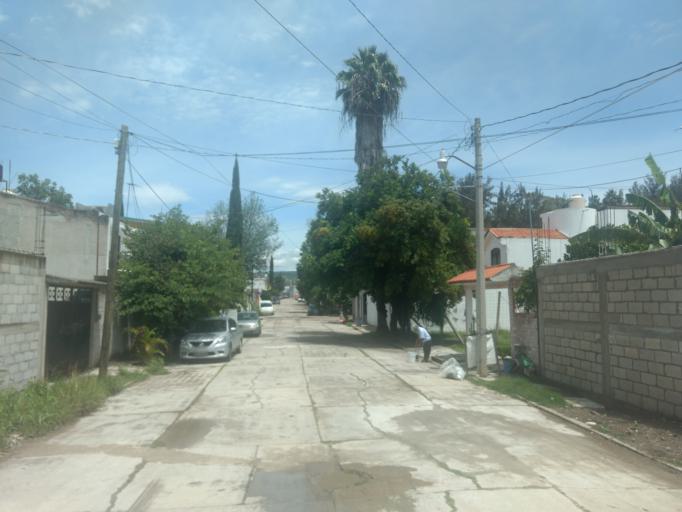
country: MX
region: Oaxaca
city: Ciudad de Huajuapam de Leon
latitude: 17.8003
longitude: -97.7776
